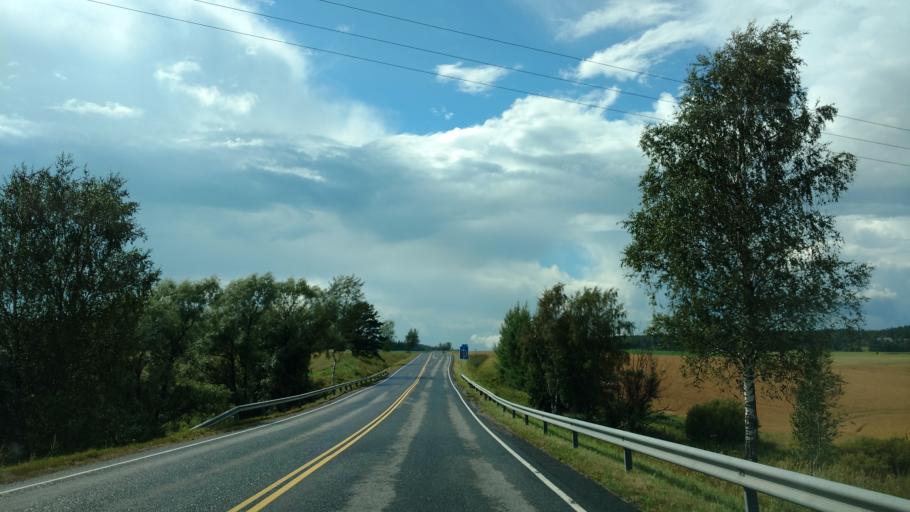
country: FI
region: Varsinais-Suomi
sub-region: Salo
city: Halikko
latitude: 60.3757
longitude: 22.9916
